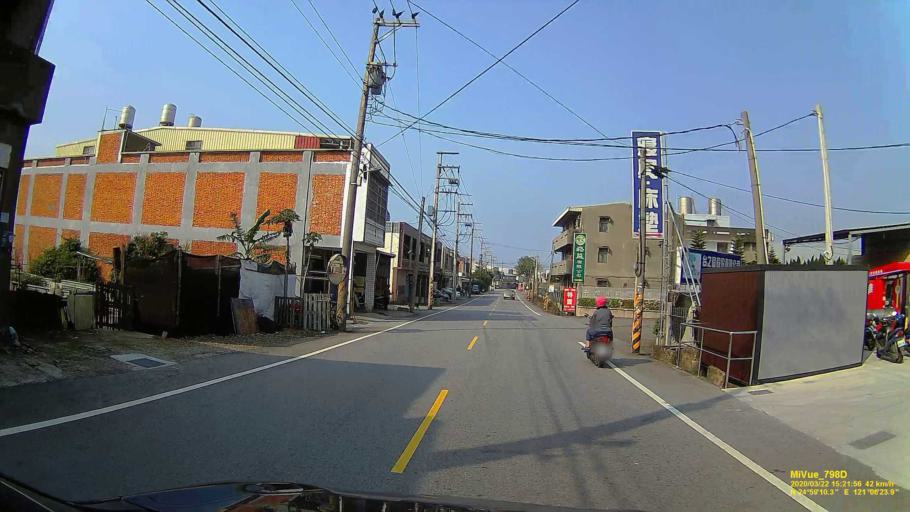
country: TW
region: Taiwan
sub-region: Hsinchu
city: Zhubei
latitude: 24.9862
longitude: 121.1067
